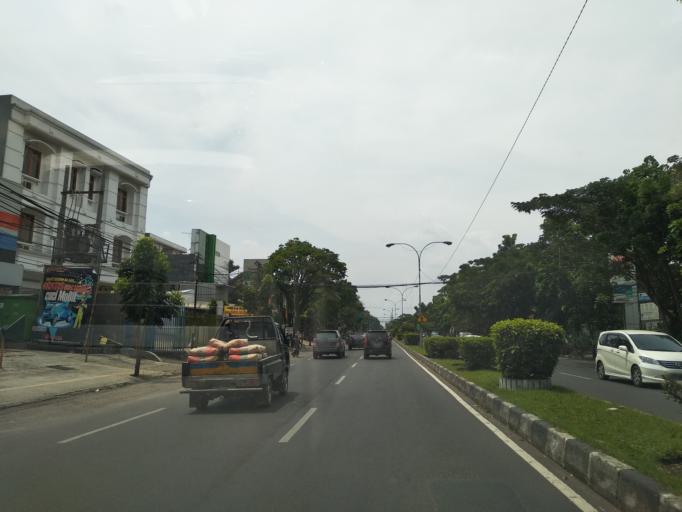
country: ID
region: West Java
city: Bandung
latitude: -6.9376
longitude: 107.6074
